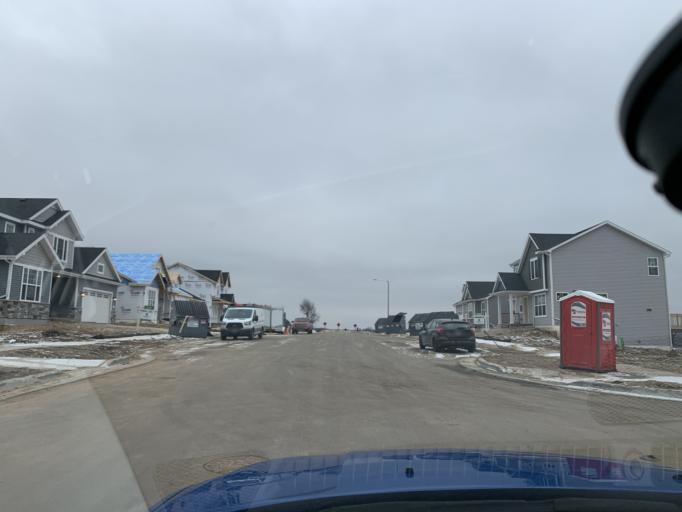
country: US
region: Wisconsin
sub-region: Dane County
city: Middleton
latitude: 43.0691
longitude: -89.5622
